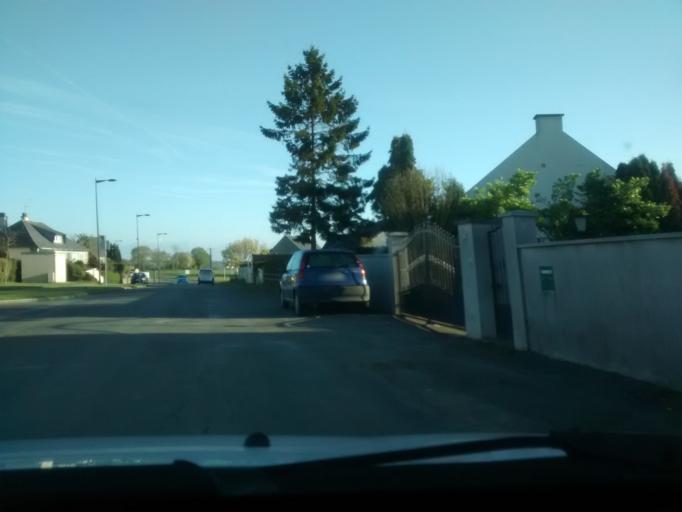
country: FR
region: Brittany
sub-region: Departement d'Ille-et-Vilaine
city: Pleine-Fougeres
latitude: 48.5362
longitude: -1.5671
